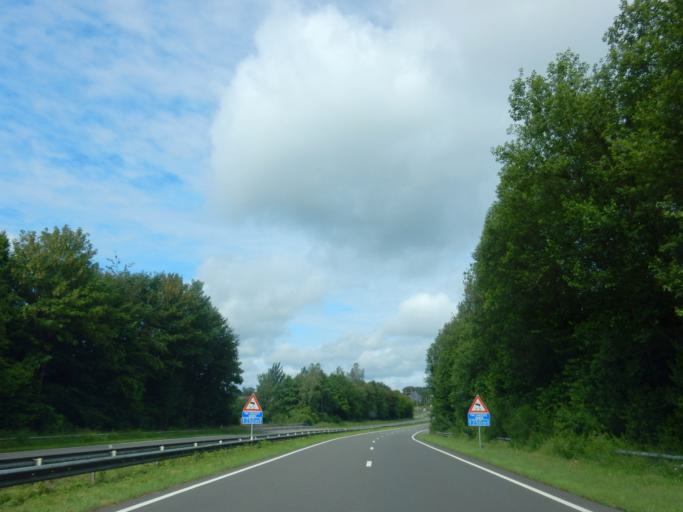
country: BE
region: Wallonia
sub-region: Province du Luxembourg
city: Paliseul
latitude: 49.8635
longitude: 5.1649
